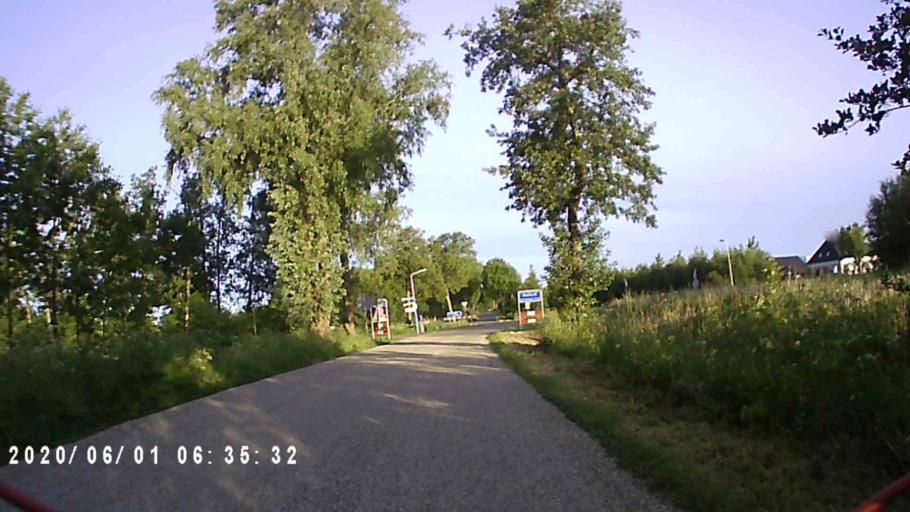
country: NL
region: Friesland
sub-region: Gemeente Kollumerland en Nieuwkruisland
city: Kollum
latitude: 53.2800
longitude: 6.1619
